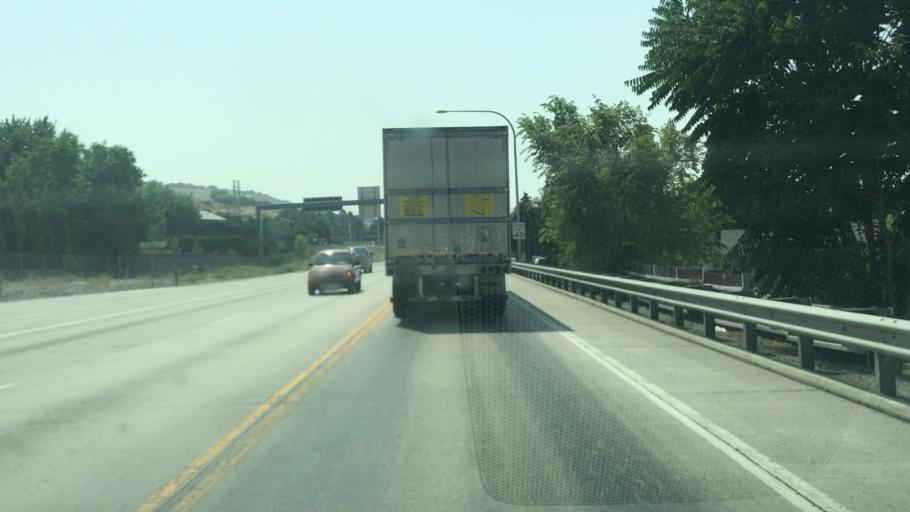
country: US
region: Washington
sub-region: Chelan County
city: Sunnyslope
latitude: 47.4672
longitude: -120.2993
